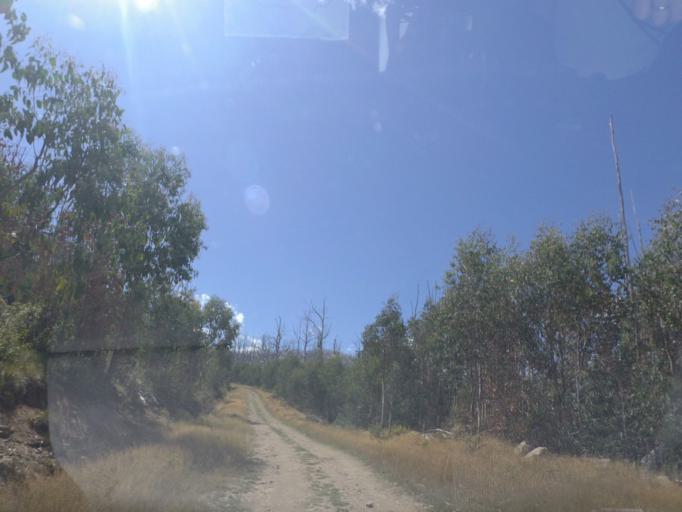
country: AU
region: Victoria
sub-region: Murrindindi
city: Alexandra
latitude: -37.4649
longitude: 145.8497
